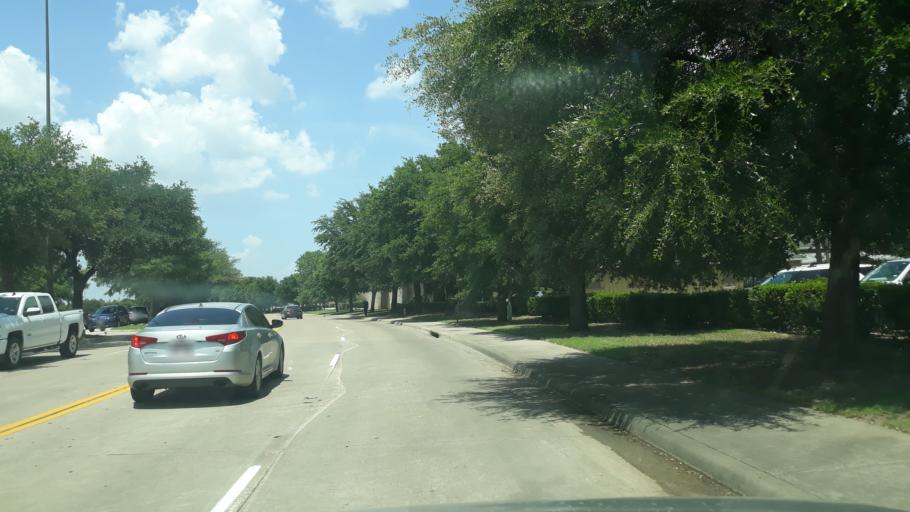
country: US
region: Texas
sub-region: Dallas County
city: Coppell
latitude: 32.9641
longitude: -97.0398
